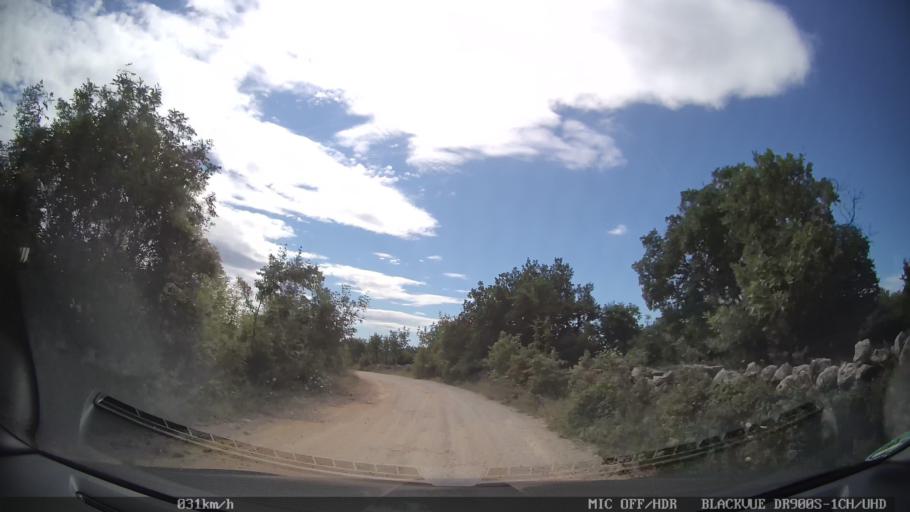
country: HR
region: Primorsko-Goranska
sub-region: Grad Krk
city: Krk
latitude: 45.0429
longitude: 14.5299
